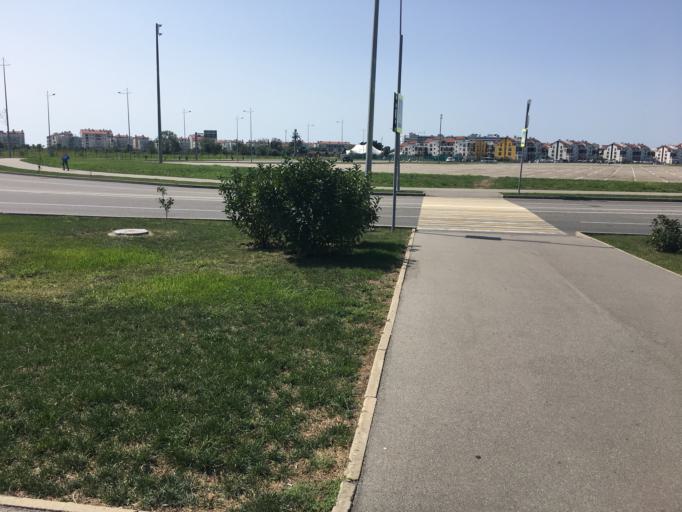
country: RU
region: Krasnodarskiy
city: Adler
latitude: 43.4120
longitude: 39.9492
